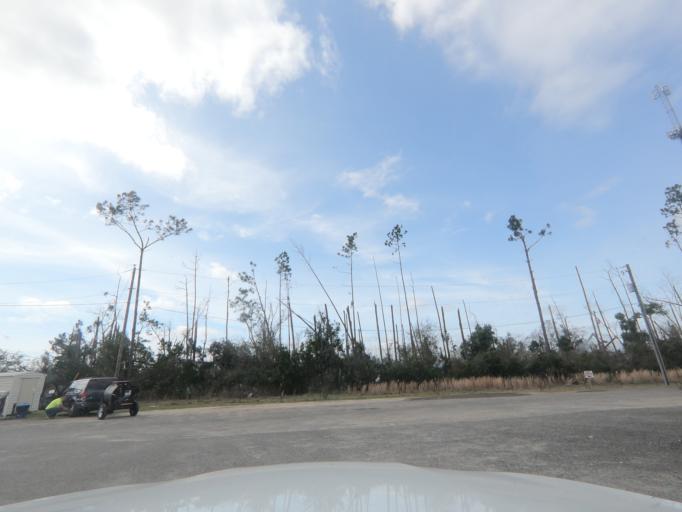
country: US
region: Florida
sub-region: Bay County
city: Youngstown
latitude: 30.3095
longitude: -85.4734
